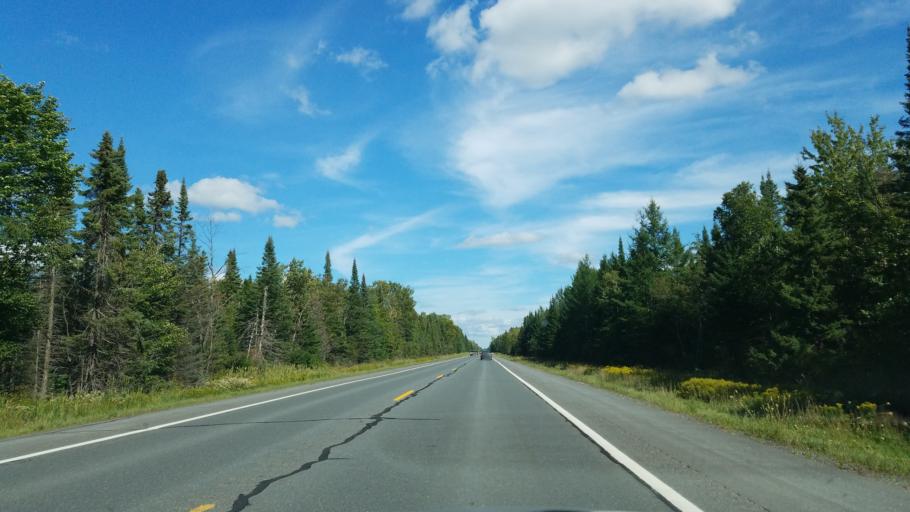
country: US
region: Michigan
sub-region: Baraga County
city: L'Anse
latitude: 46.5788
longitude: -88.4367
